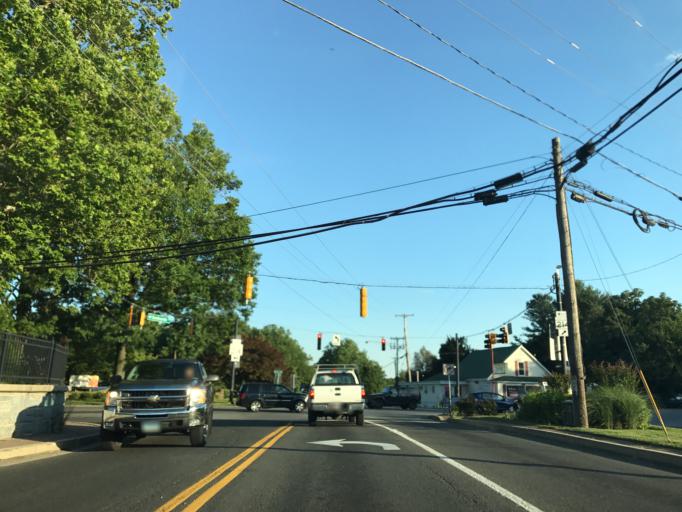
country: US
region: Maryland
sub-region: Anne Arundel County
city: Davidsonville
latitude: 38.9233
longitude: -76.6285
